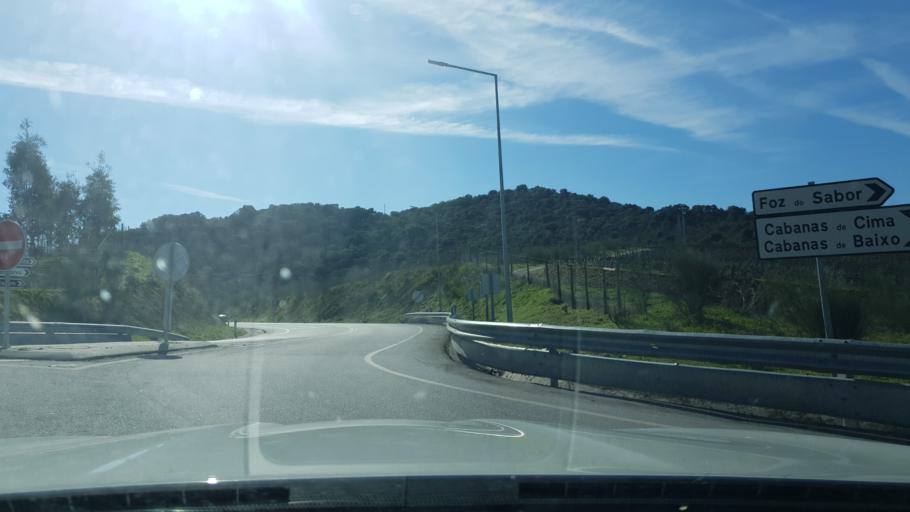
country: PT
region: Braganca
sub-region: Torre de Moncorvo
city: Torre de Moncorvo
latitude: 41.2144
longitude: -7.0898
